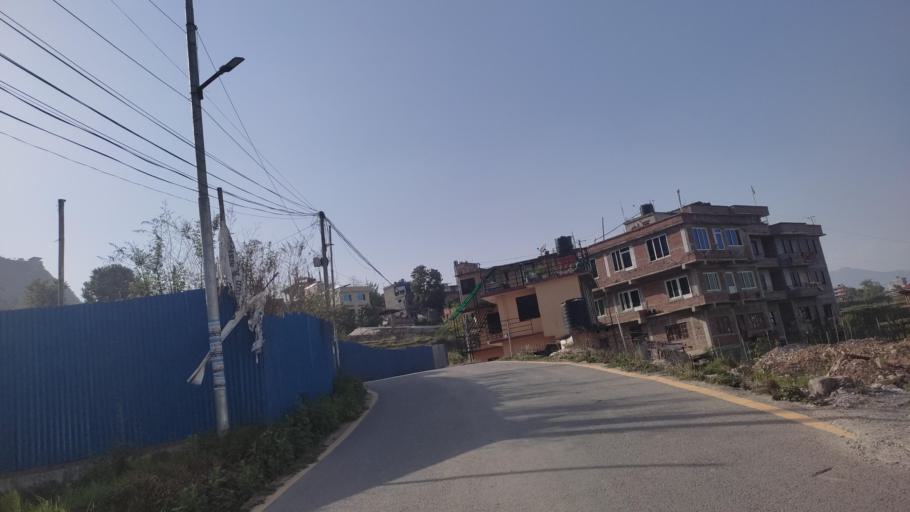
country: NP
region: Central Region
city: Kirtipur
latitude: 27.6500
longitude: 85.2777
